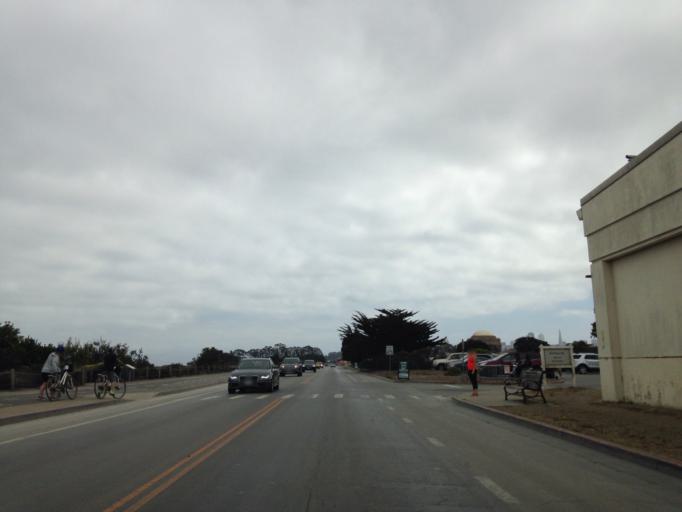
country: US
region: California
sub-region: San Francisco County
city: San Francisco
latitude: 37.8036
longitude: -122.4591
